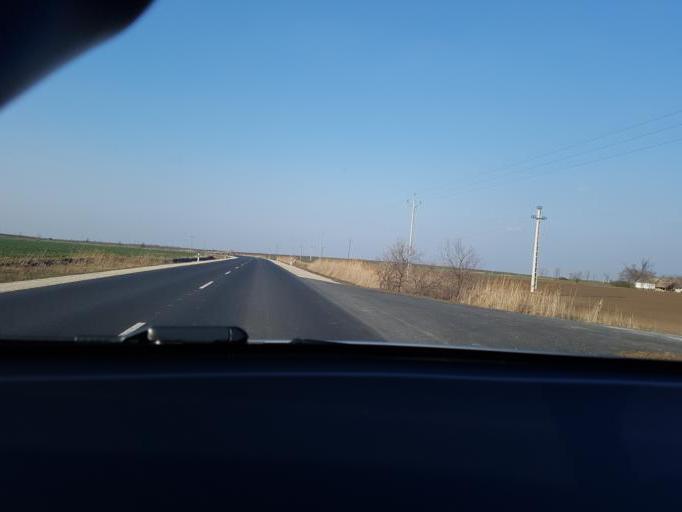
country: HU
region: Csongrad
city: Csanadpalota
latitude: 46.2052
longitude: 20.7177
